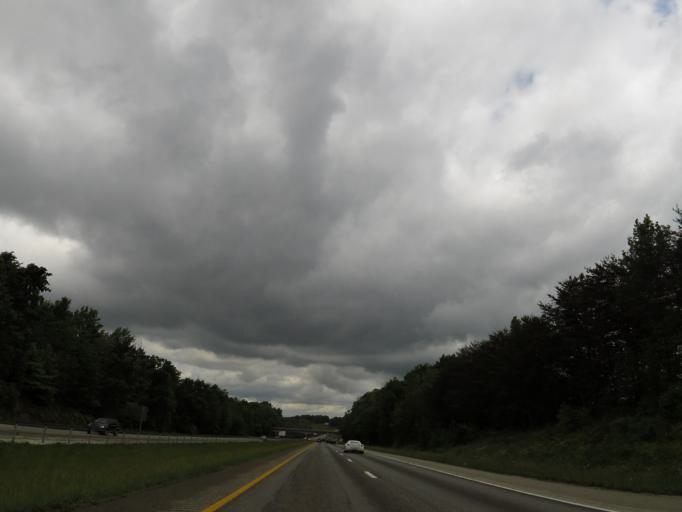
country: US
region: Kentucky
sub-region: Whitley County
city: Corbin
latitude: 36.9418
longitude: -84.1238
